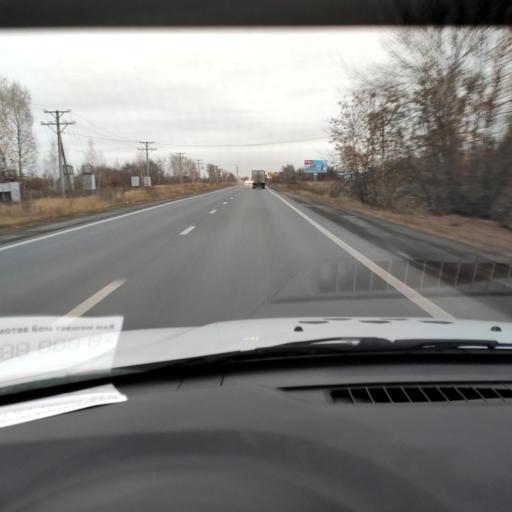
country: RU
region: Samara
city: Tol'yatti
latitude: 53.5512
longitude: 49.3717
